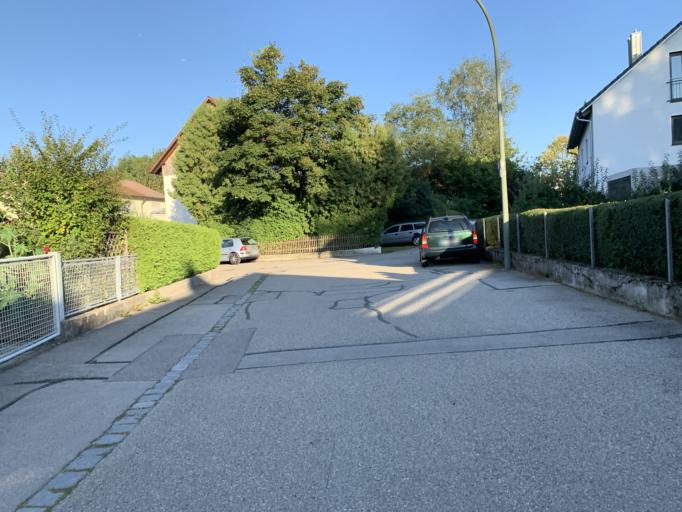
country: DE
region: Bavaria
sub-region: Upper Bavaria
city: Freising
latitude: 48.3847
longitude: 11.7526
